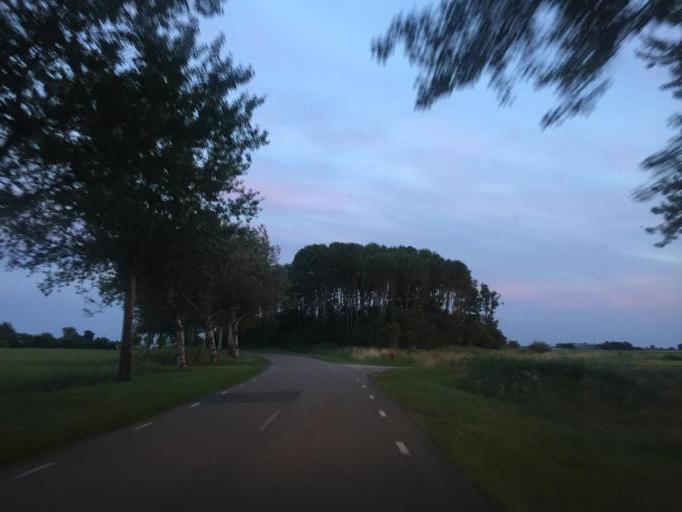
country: NL
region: Friesland
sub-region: Gemeente Dongeradeel
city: Anjum
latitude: 53.3994
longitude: 6.0856
